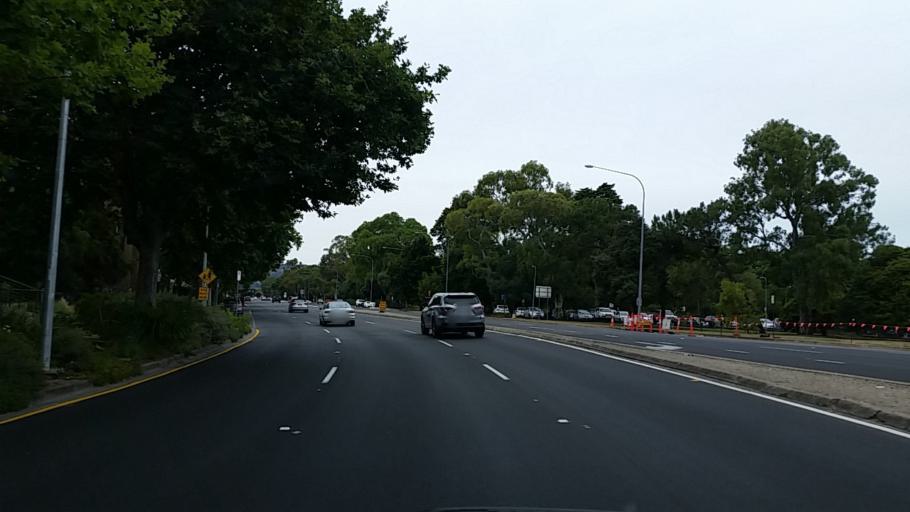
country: AU
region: South Australia
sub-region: Adelaide
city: Adelaide
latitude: -34.9225
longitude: 138.6158
